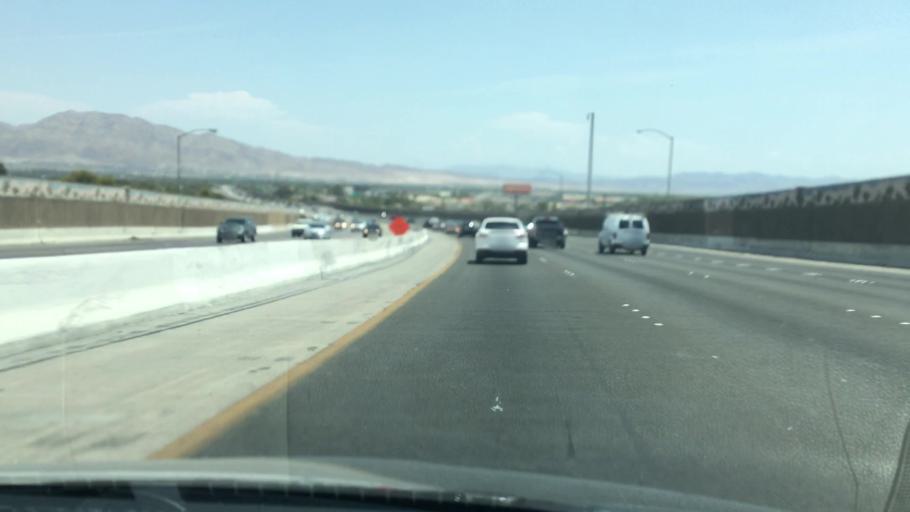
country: US
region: Nevada
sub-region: Clark County
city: Las Vegas
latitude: 36.1683
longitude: -115.1261
